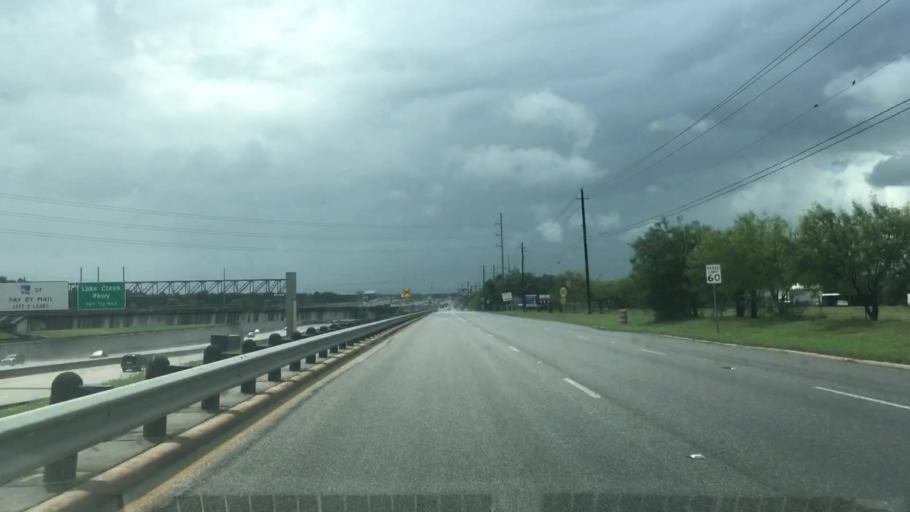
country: US
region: Texas
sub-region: Williamson County
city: Jollyville
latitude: 30.4785
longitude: -97.7597
